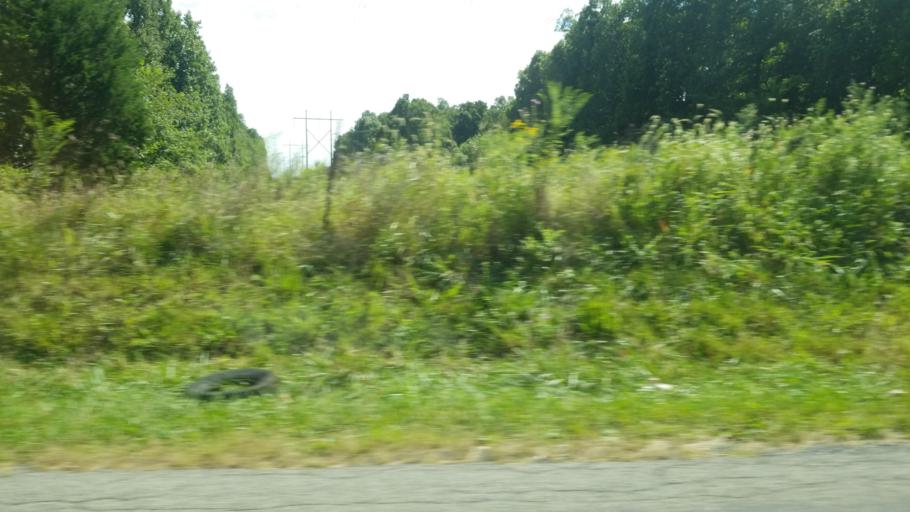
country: US
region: Illinois
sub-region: Williamson County
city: Johnston City
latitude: 37.7903
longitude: -88.8397
